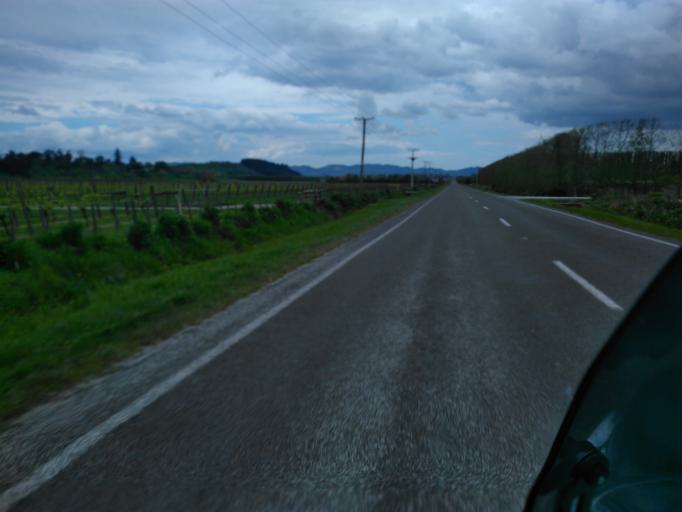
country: NZ
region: Gisborne
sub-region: Gisborne District
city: Gisborne
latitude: -38.6442
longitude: 177.8690
